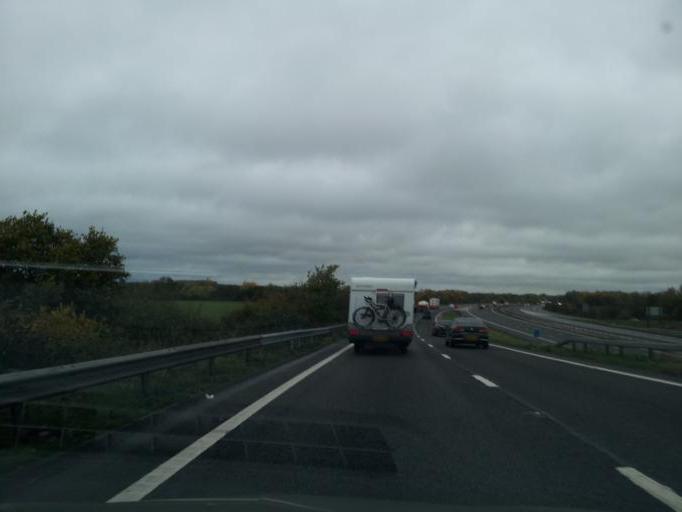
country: GB
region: England
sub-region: Oxfordshire
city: Bicester
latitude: 51.8699
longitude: -1.1999
